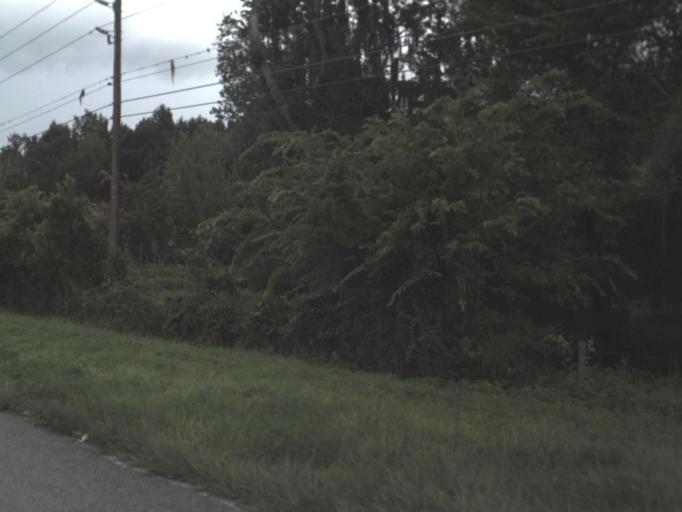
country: US
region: Florida
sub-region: Pasco County
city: Wesley Chapel
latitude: 28.3239
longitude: -82.3829
